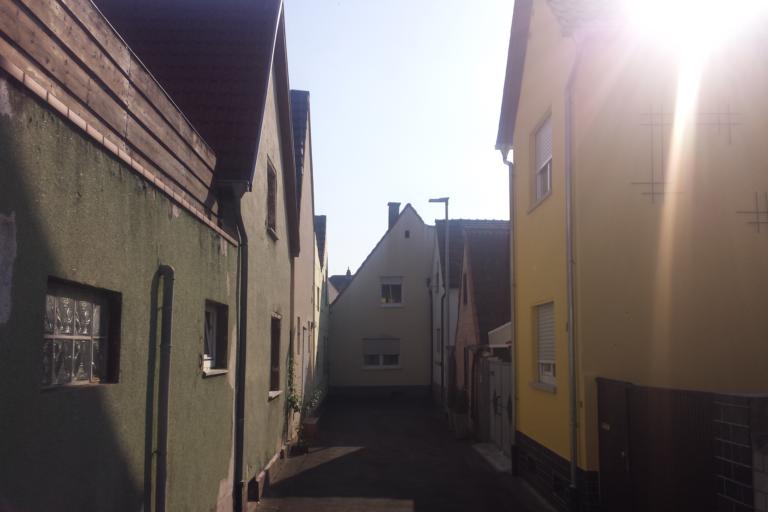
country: DE
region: Rheinland-Pfalz
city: Waldsee
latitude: 49.3963
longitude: 8.4393
